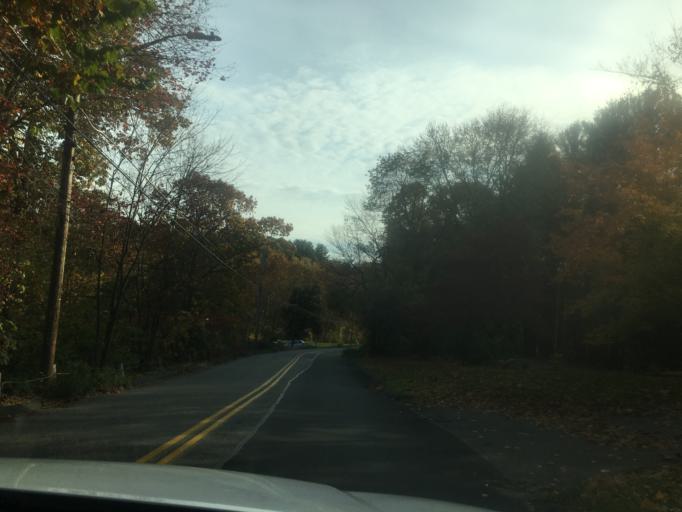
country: US
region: Connecticut
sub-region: Hartford County
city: Broad Brook
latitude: 41.8814
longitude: -72.5742
